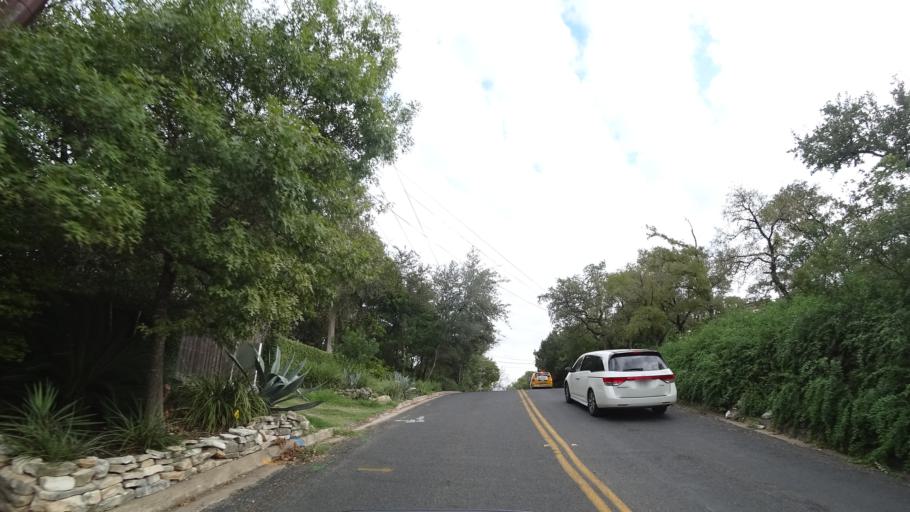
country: US
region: Texas
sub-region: Travis County
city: Rollingwood
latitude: 30.2822
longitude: -97.7845
